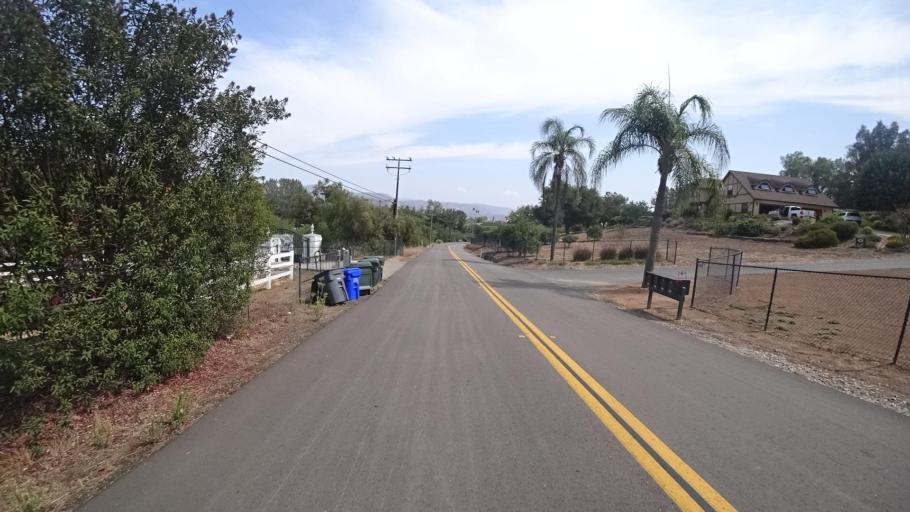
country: US
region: California
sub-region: San Diego County
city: Escondido
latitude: 33.0939
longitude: -117.0361
